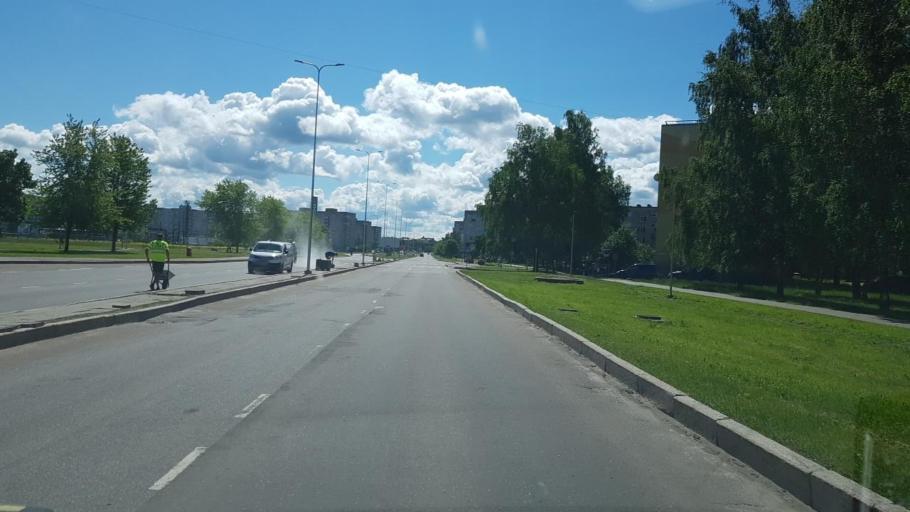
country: EE
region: Ida-Virumaa
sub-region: Narva linn
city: Narva
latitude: 59.3897
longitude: 28.1727
